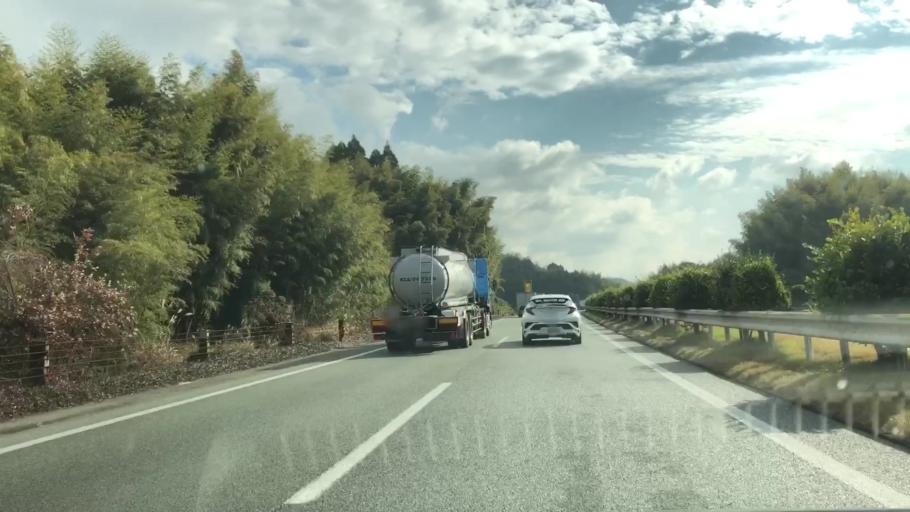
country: JP
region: Fukuoka
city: Setakamachi-takayanagi
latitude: 33.1090
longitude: 130.5329
